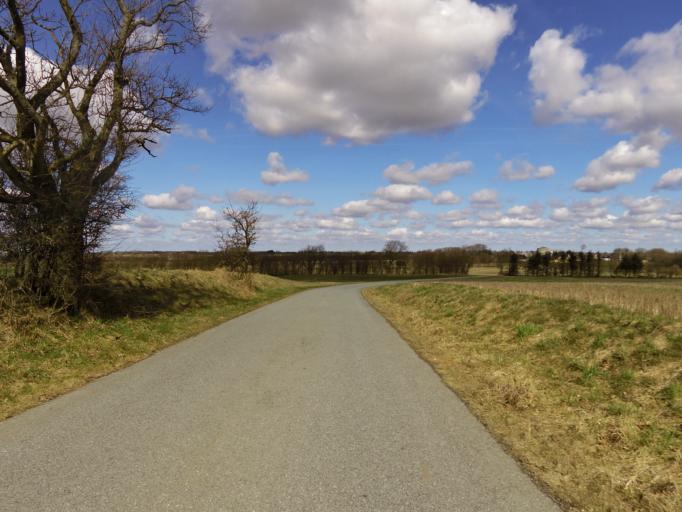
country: DK
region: South Denmark
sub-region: Tonder Kommune
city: Toftlund
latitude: 55.1596
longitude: 9.0487
